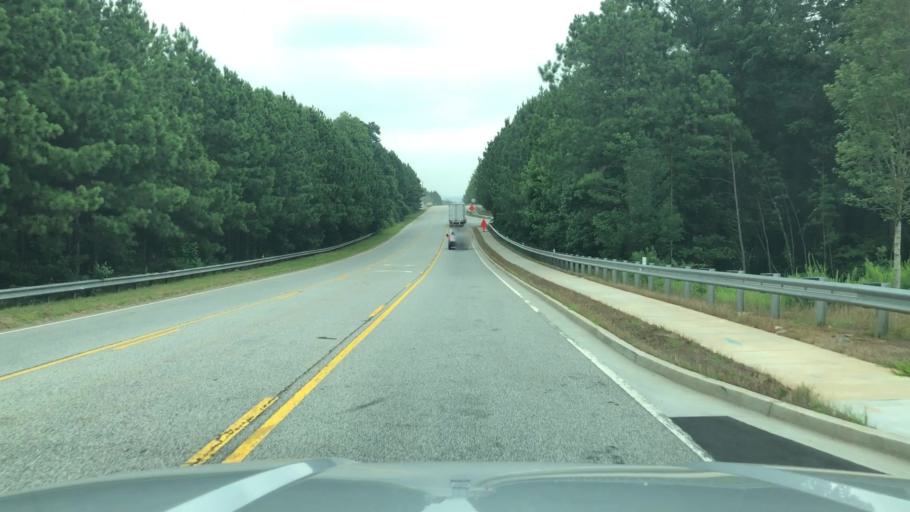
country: US
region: Georgia
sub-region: Cobb County
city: Mableton
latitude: 33.7728
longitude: -84.5787
